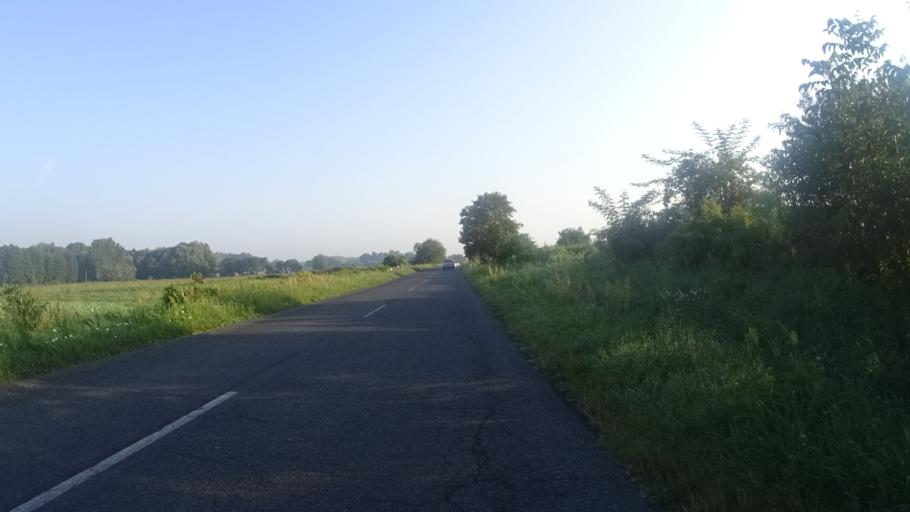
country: HU
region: Zala
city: Zalakomar
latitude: 46.5689
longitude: 17.1775
